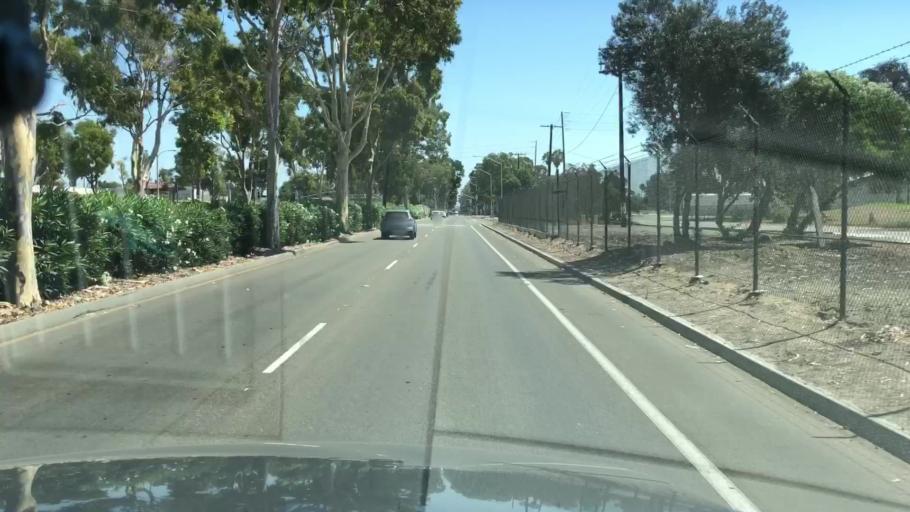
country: US
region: California
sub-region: Ventura County
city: Channel Islands Beach
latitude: 34.1757
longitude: -119.2110
